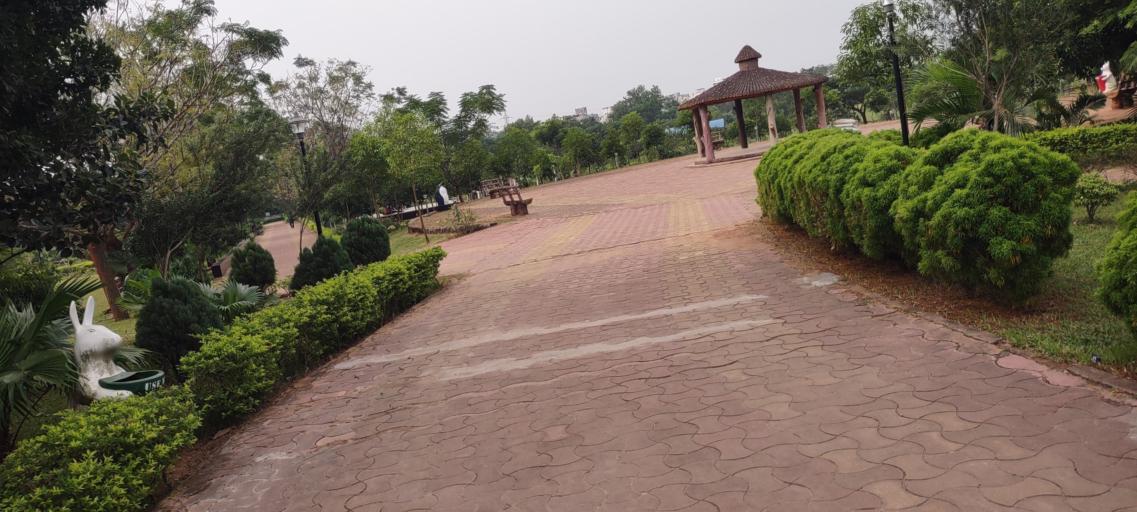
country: IN
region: Odisha
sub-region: Khordha
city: Bhubaneshwar
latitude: 20.2785
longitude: 85.7659
